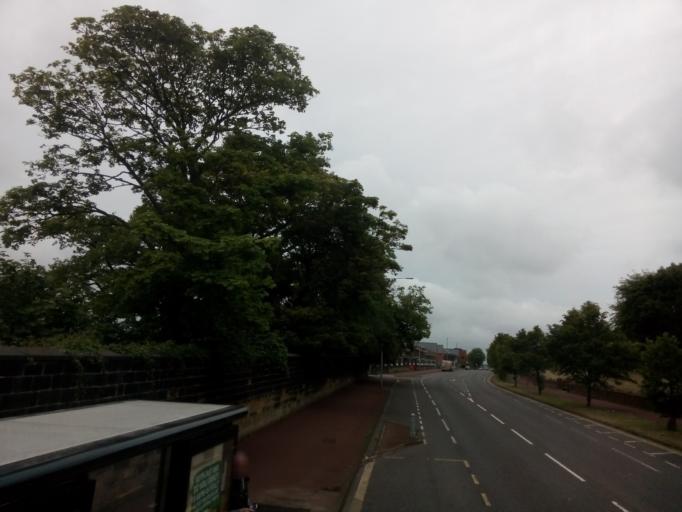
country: GB
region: England
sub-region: Gateshead
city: Gateshead
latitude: 54.9443
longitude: -1.5999
